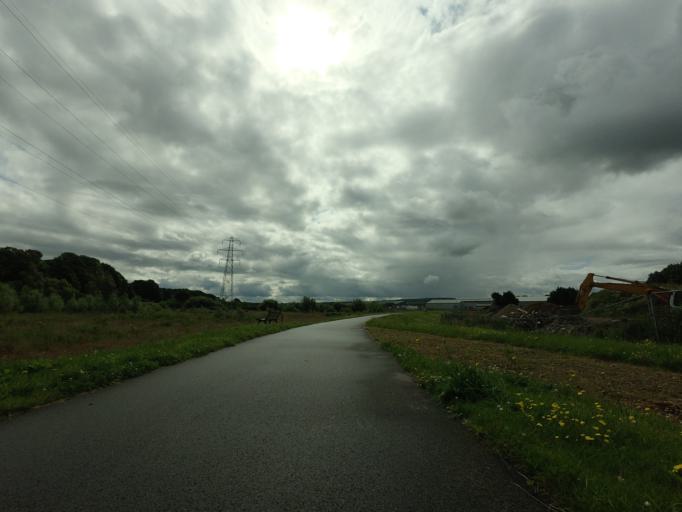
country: GB
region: Scotland
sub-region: Moray
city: Elgin
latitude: 57.6495
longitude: -3.2849
